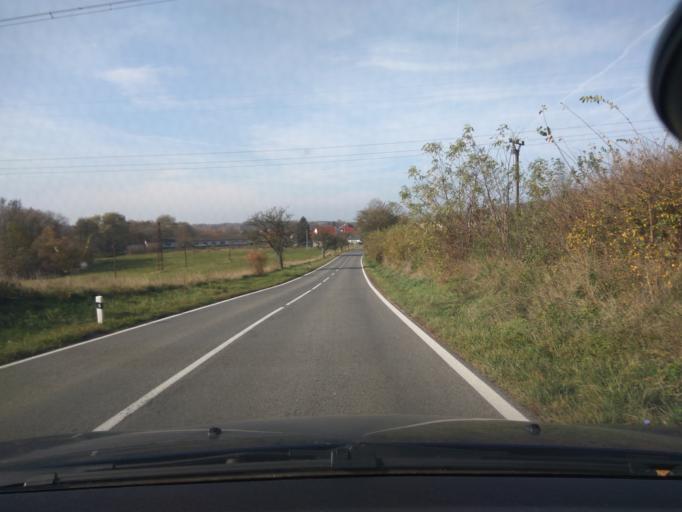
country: SK
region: Nitriansky
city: Brezova pod Bradlom
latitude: 48.6208
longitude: 17.4487
